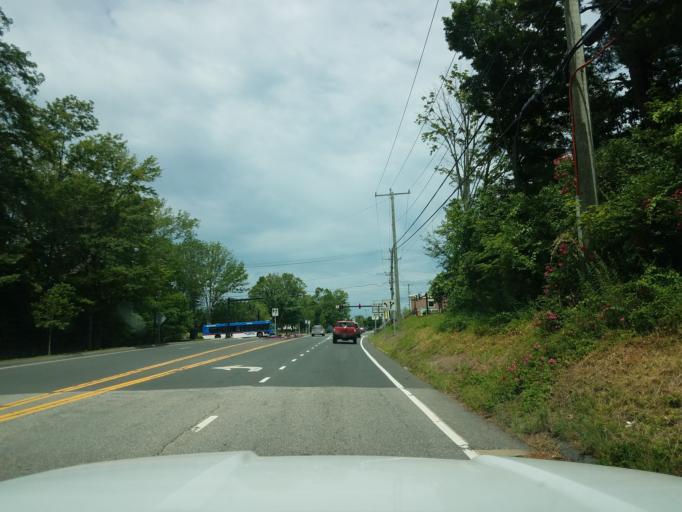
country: US
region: Connecticut
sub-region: Tolland County
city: Storrs
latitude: 41.8006
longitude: -72.2402
